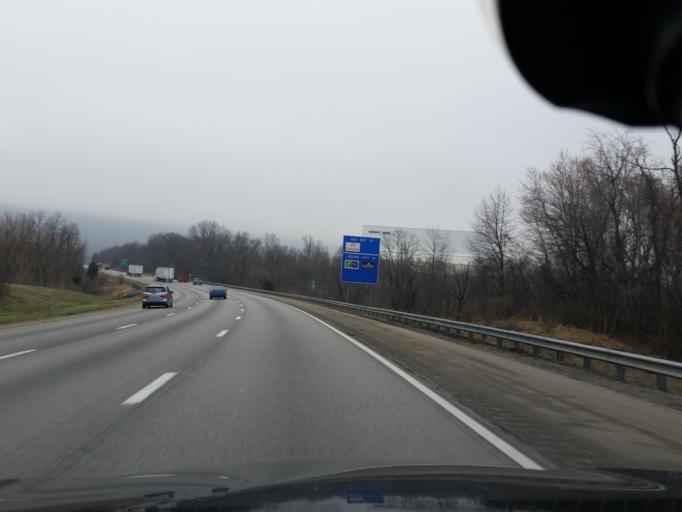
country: US
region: Pennsylvania
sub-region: Cumberland County
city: Enola
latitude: 40.2795
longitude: -76.9833
